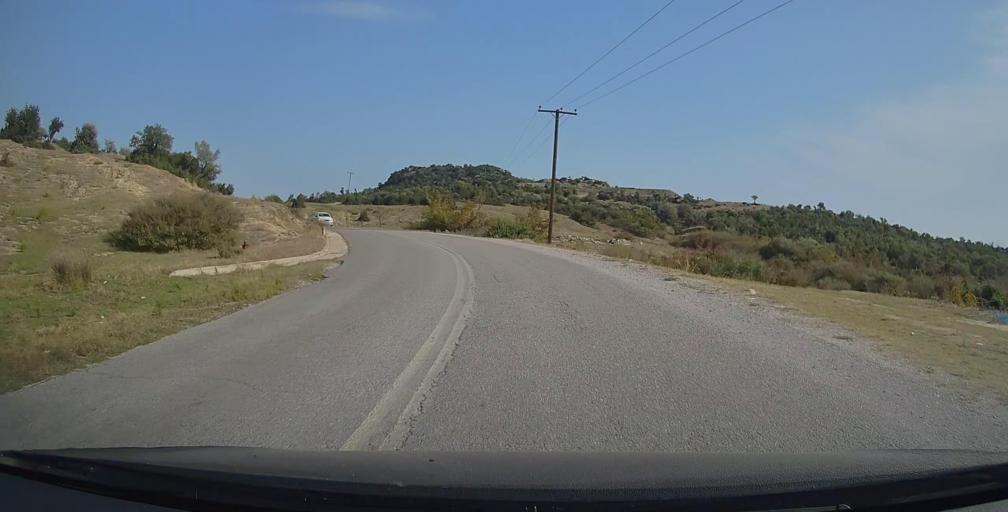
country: GR
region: Central Macedonia
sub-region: Nomos Chalkidikis
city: Sykia
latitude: 40.0236
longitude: 23.9884
